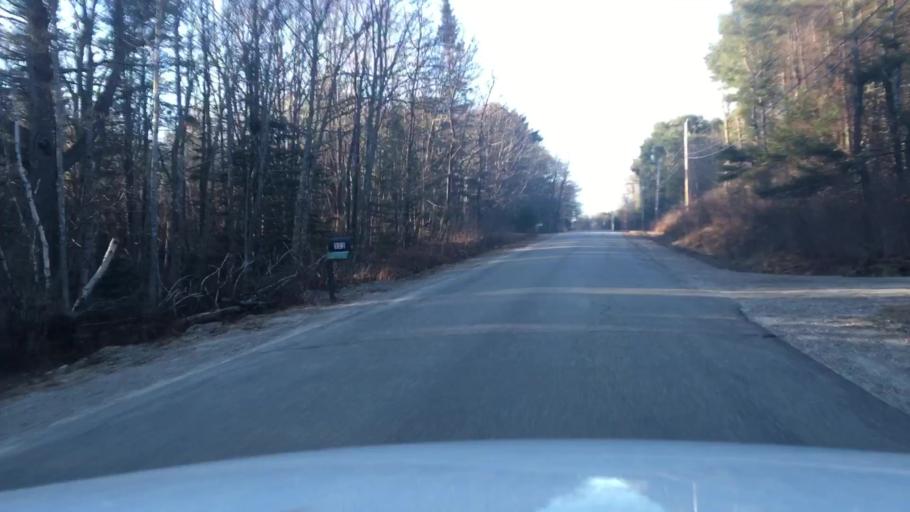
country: US
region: Maine
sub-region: Cumberland County
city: Brunswick
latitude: 43.8750
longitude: -69.9146
